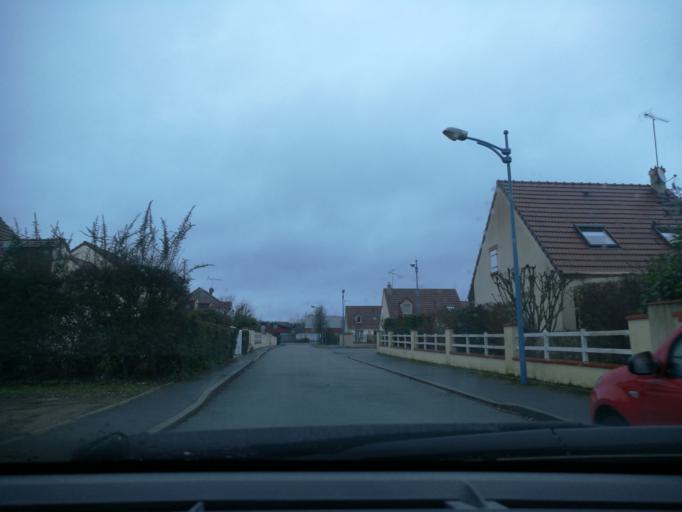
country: FR
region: Centre
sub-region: Departement du Loiret
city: Fleury-les-Aubrais
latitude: 47.9378
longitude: 1.9082
